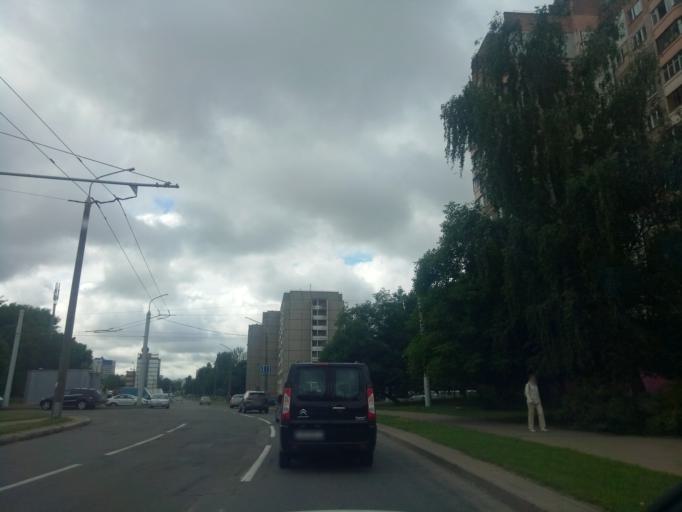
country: BY
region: Minsk
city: Novoye Medvezhino
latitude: 53.9094
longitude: 27.5000
